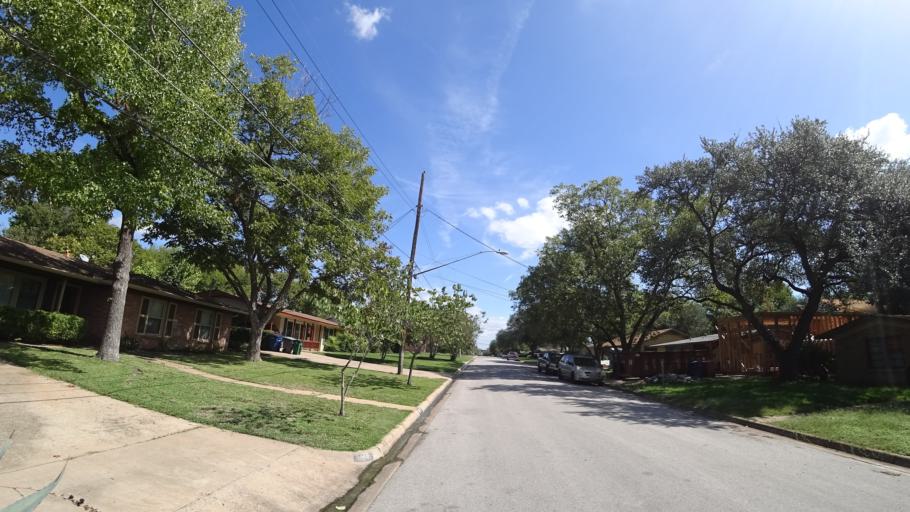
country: US
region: Texas
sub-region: Travis County
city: Austin
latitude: 30.3398
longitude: -97.7288
